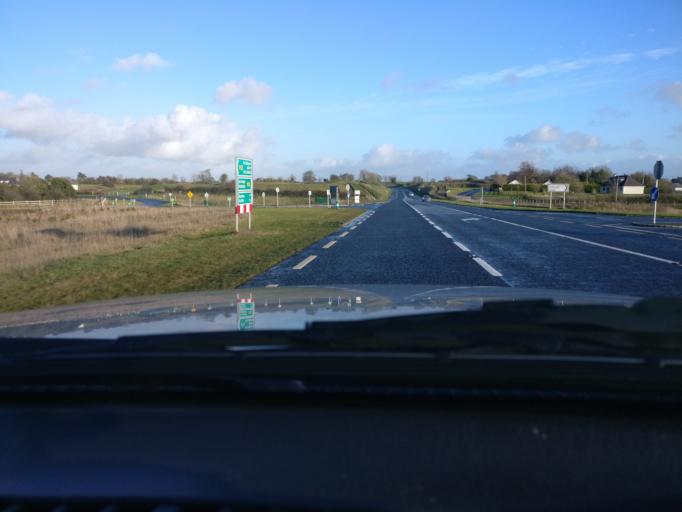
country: IE
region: Leinster
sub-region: An Iarmhi
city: Rathwire
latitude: 53.5570
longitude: -7.2270
